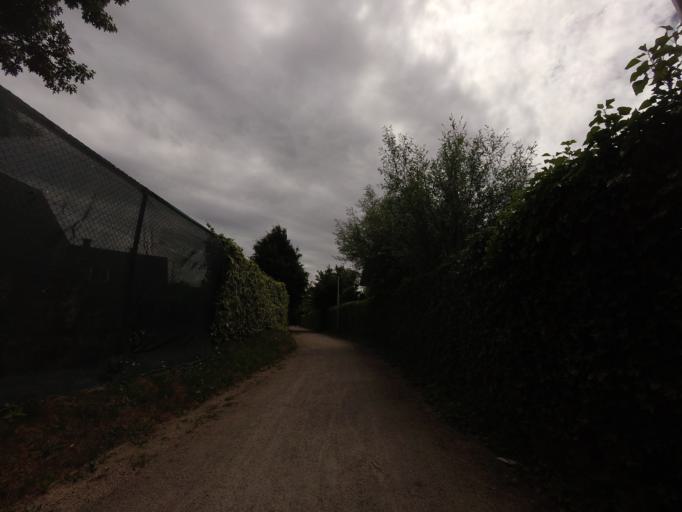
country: BE
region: Flanders
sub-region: Provincie Antwerpen
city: Duffel
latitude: 51.0878
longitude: 4.4856
